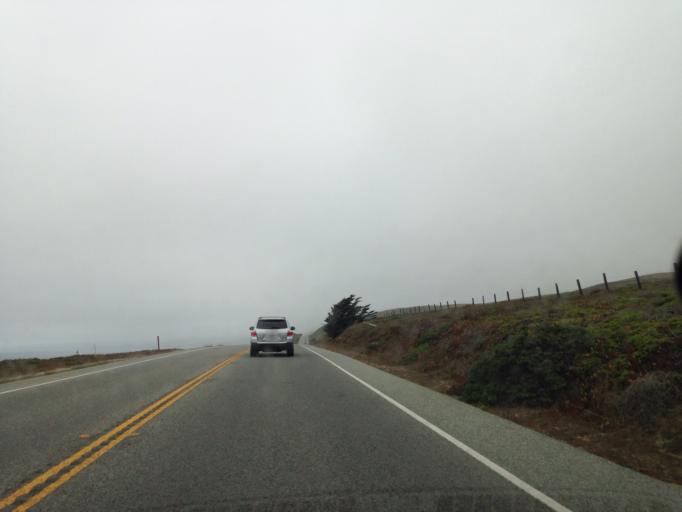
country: US
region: California
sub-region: San Mateo County
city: Half Moon Bay
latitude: 37.3062
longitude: -122.4046
